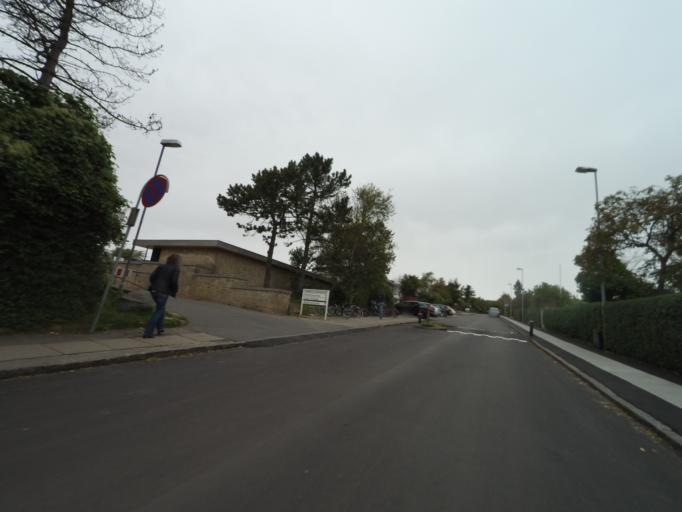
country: DK
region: Central Jutland
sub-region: Arhus Kommune
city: Stavtrup
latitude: 56.1582
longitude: 10.1583
